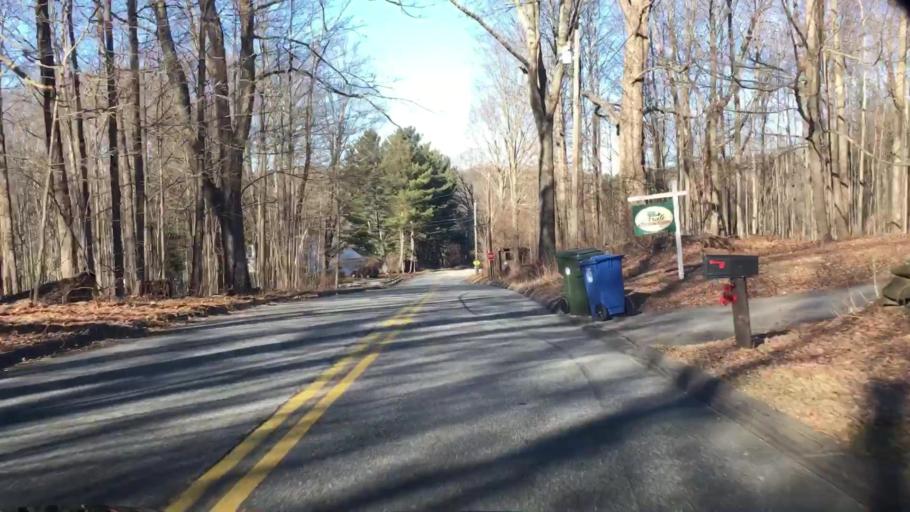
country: US
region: Connecticut
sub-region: Tolland County
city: Tolland
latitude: 41.8972
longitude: -72.3913
